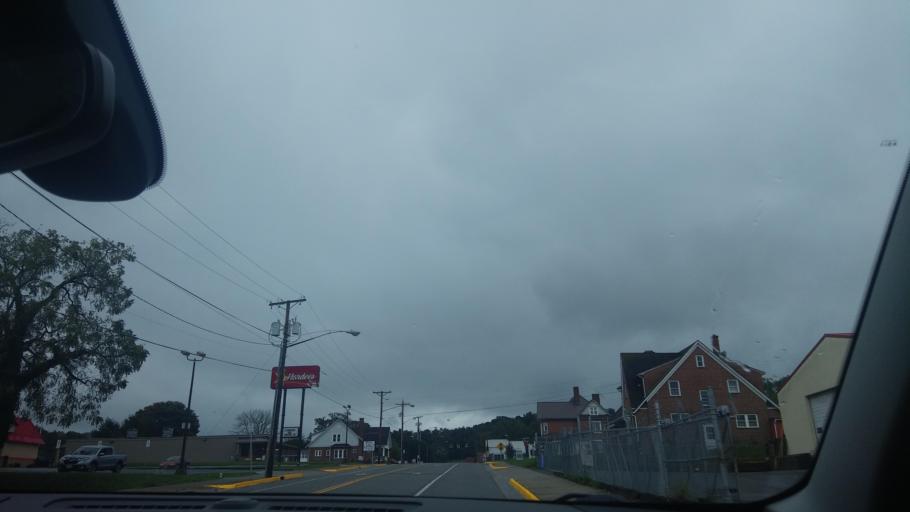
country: US
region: Virginia
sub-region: City of Galax
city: Galax
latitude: 36.6594
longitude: -80.9238
